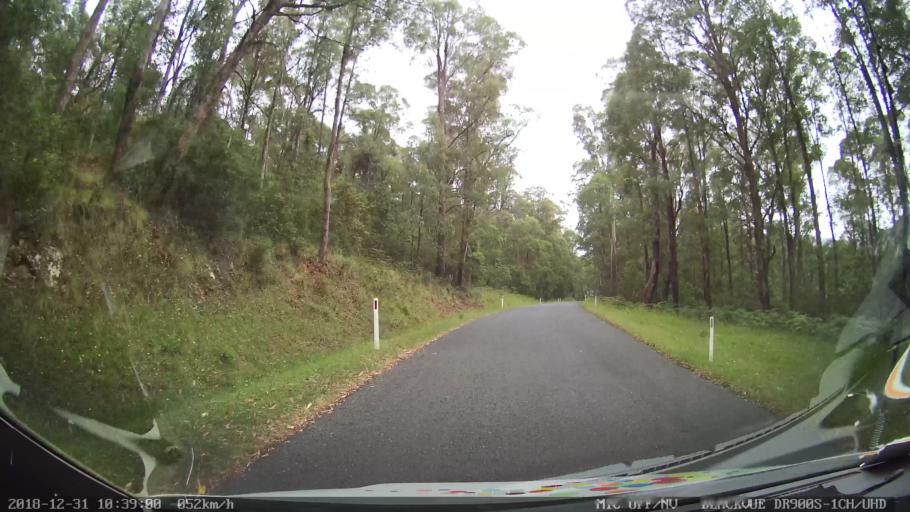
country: AU
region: New South Wales
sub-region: Snowy River
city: Jindabyne
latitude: -36.4031
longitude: 148.1764
